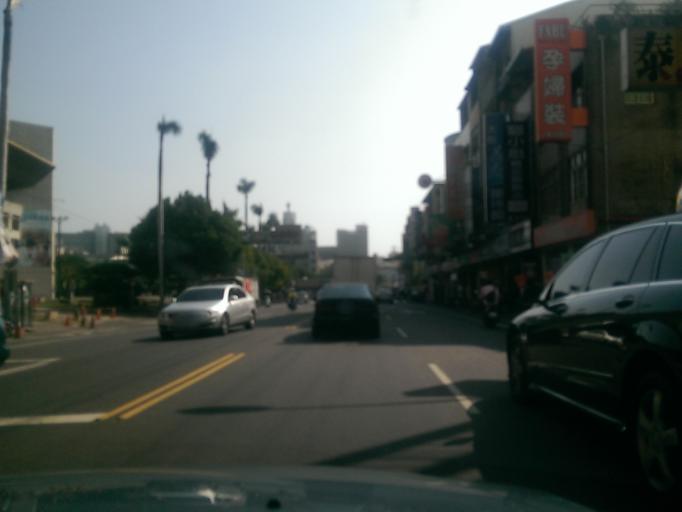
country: TW
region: Taiwan
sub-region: Changhua
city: Chang-hua
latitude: 24.0762
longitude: 120.5442
